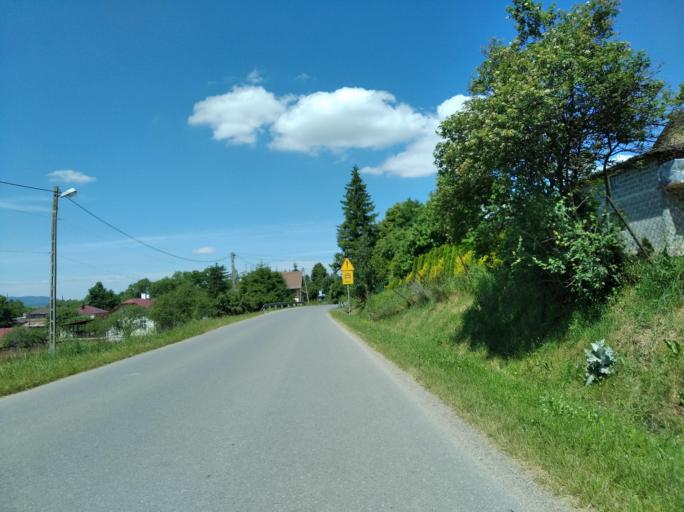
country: PL
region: Subcarpathian Voivodeship
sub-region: Powiat jasielski
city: Nowy Zmigrod
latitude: 49.6214
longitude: 21.5453
